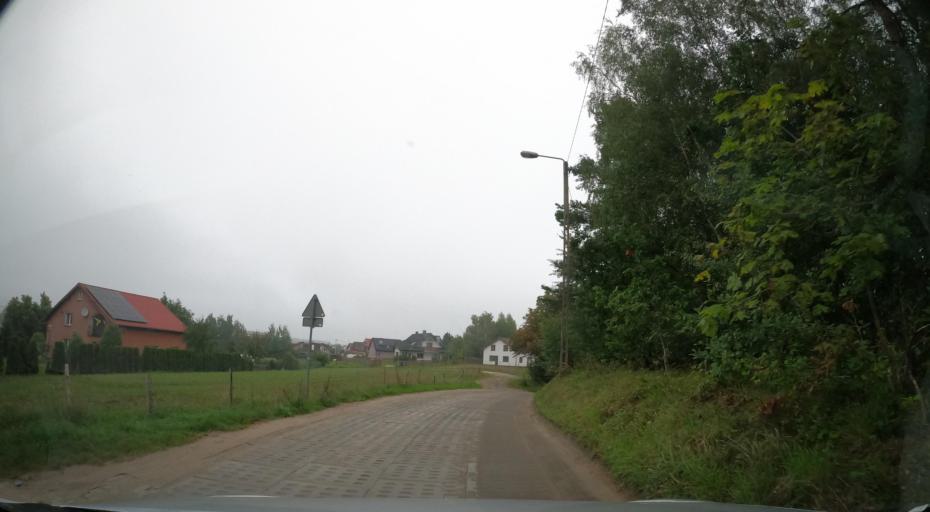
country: PL
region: Pomeranian Voivodeship
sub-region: Powiat kartuski
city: Chwaszczyno
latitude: 54.4183
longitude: 18.4395
